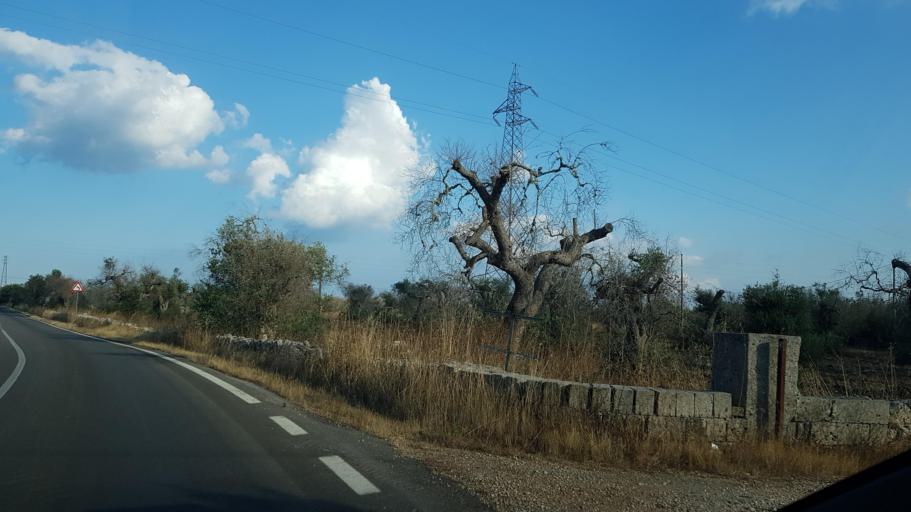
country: IT
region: Apulia
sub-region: Provincia di Lecce
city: Castiglione
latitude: 39.9840
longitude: 18.3633
